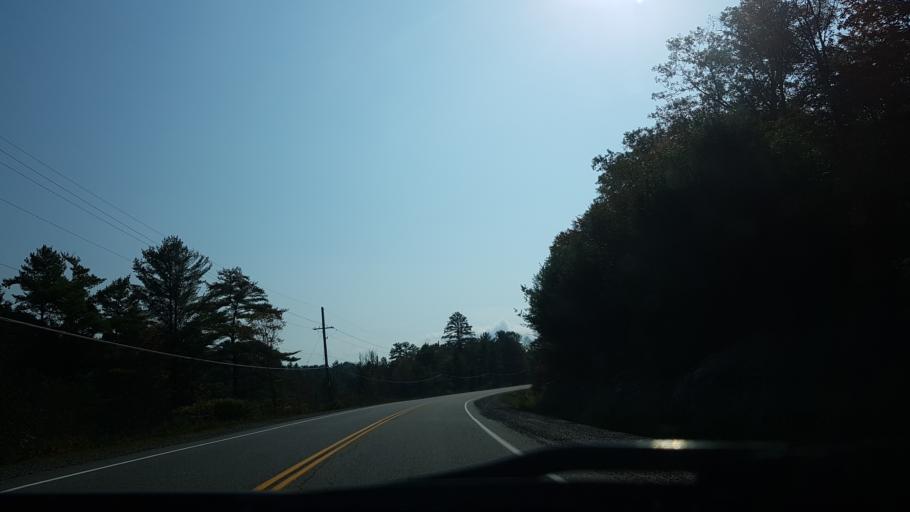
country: CA
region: Ontario
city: Bracebridge
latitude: 44.9899
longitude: -79.2797
